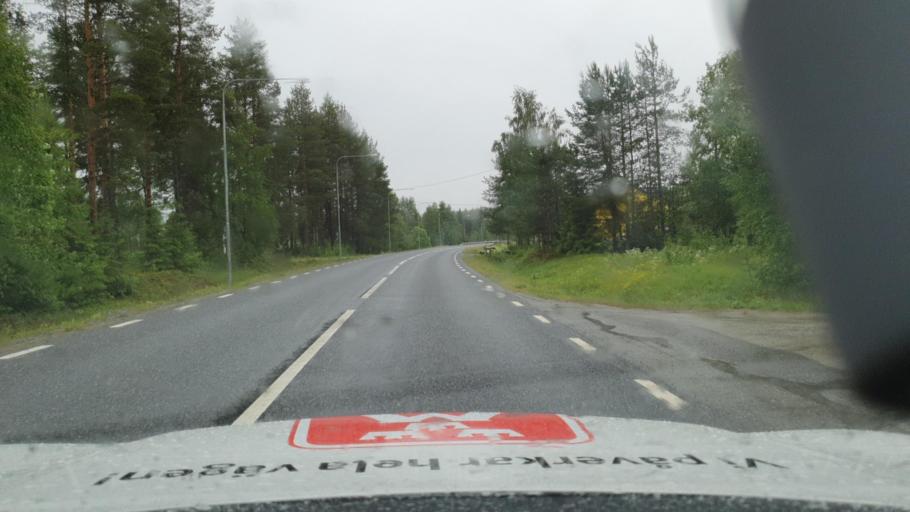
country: SE
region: Vaesterbotten
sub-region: Asele Kommun
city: Asele
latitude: 64.0882
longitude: 17.3243
